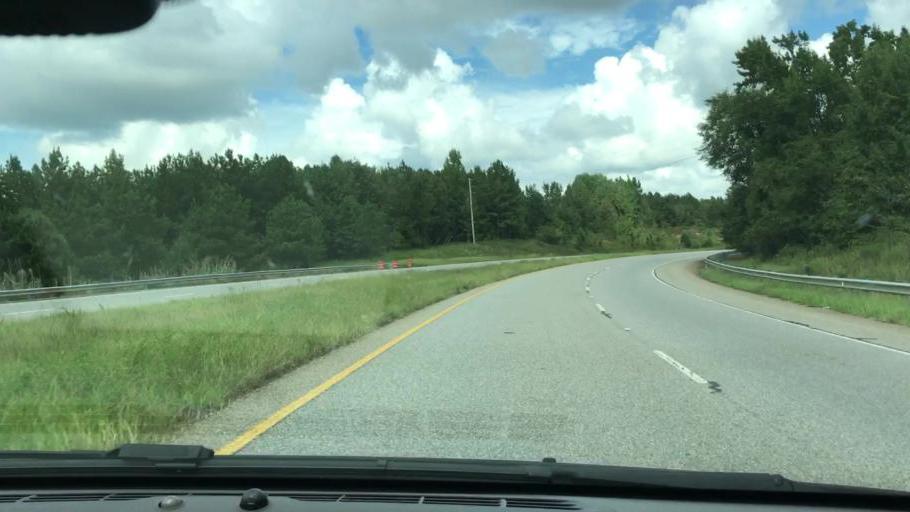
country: US
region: Georgia
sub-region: Stewart County
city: Lumpkin
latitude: 32.0890
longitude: -84.8091
